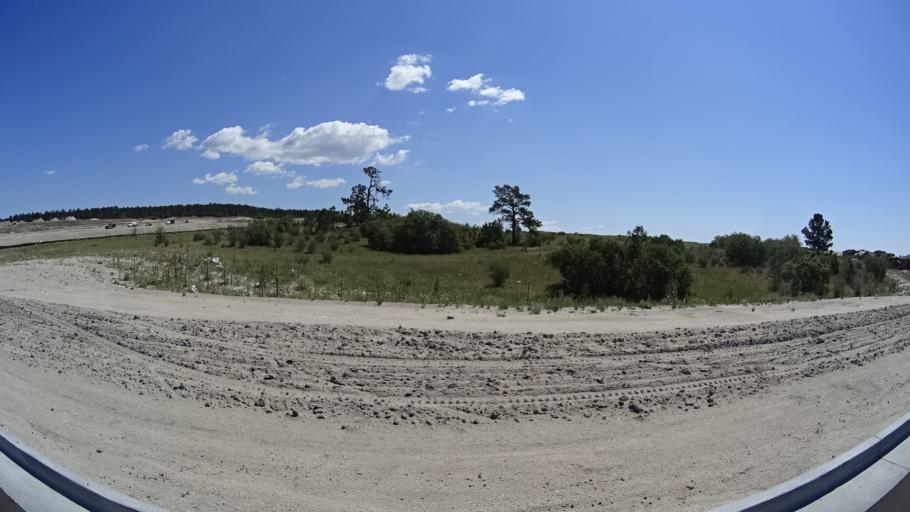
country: US
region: Colorado
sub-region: El Paso County
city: Black Forest
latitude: 38.9795
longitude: -104.7379
